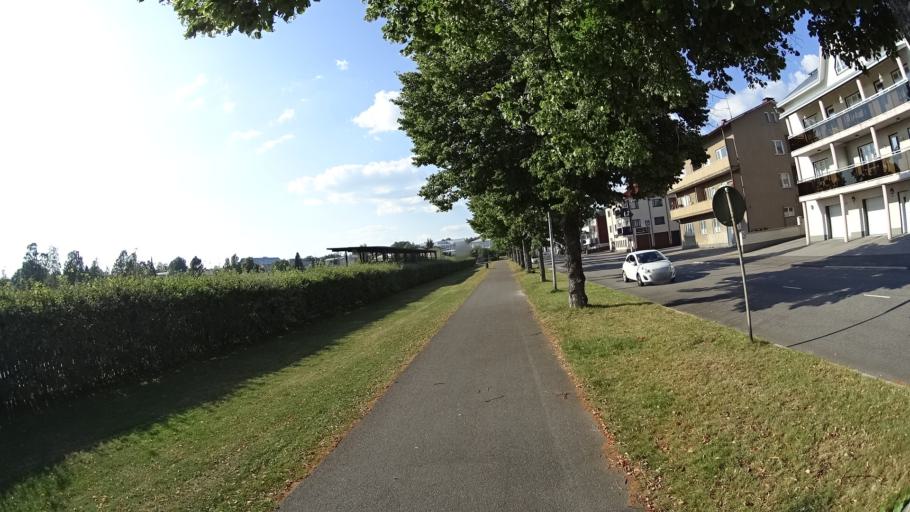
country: FI
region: Uusimaa
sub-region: Porvoo
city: Porvoo
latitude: 60.3936
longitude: 25.6744
